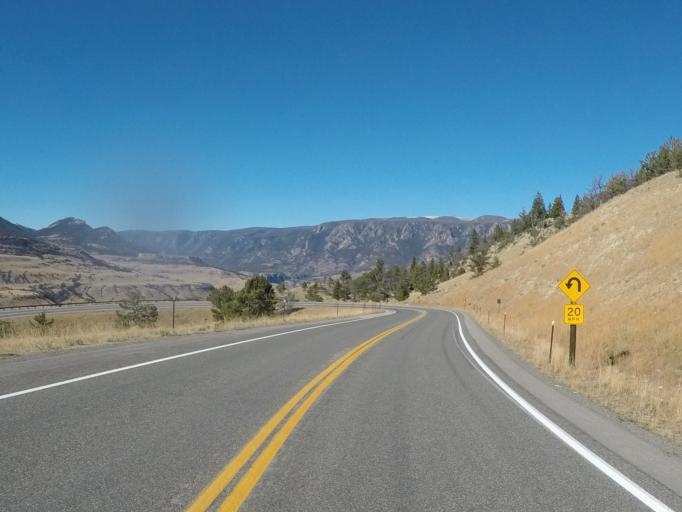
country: US
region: Wyoming
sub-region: Park County
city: Cody
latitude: 44.7546
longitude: -109.3995
